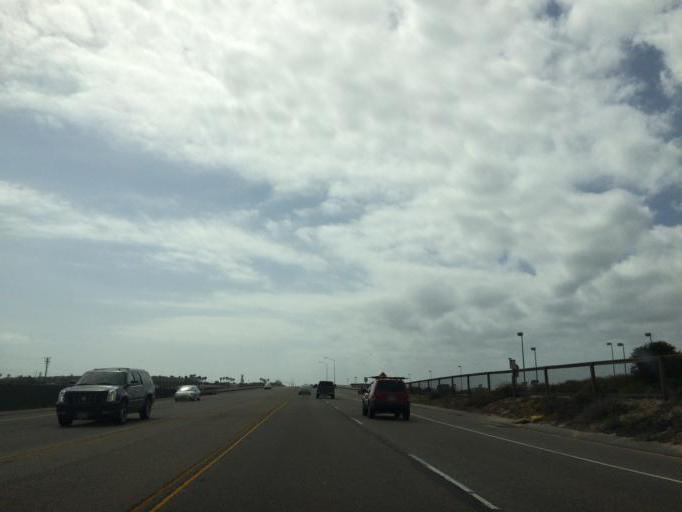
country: US
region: California
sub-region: Orange County
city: Huntington Beach
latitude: 33.6866
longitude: -118.0387
